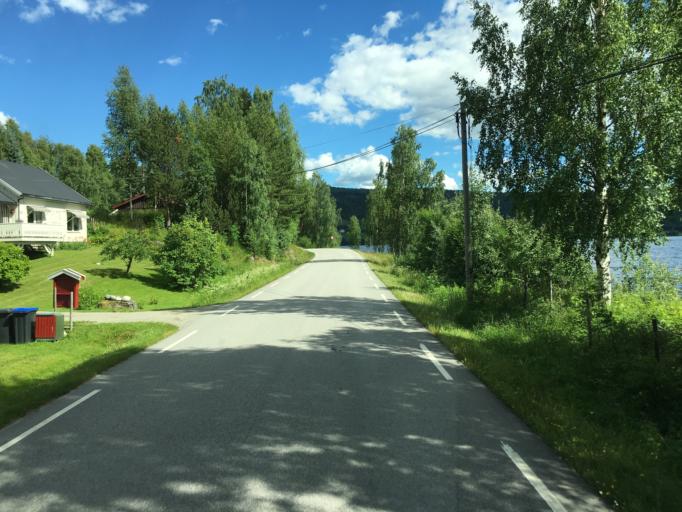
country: NO
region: Oppland
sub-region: Sondre Land
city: Hov
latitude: 60.5989
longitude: 10.3122
